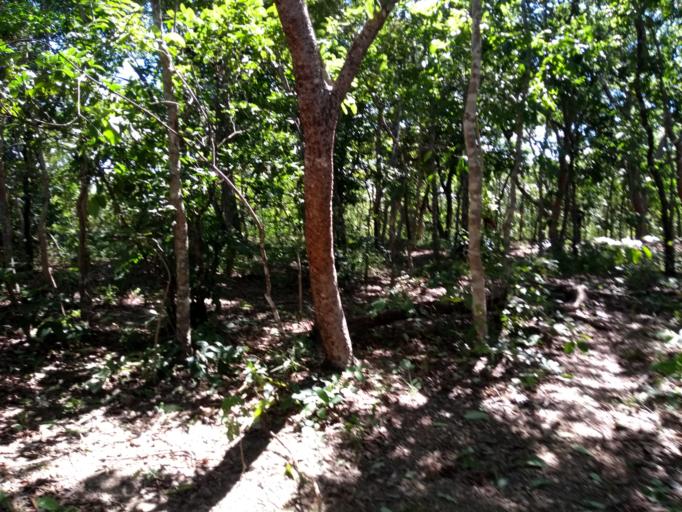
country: BR
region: Goias
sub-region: Goianesia
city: Goianesia
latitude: -15.3336
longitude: -48.8546
